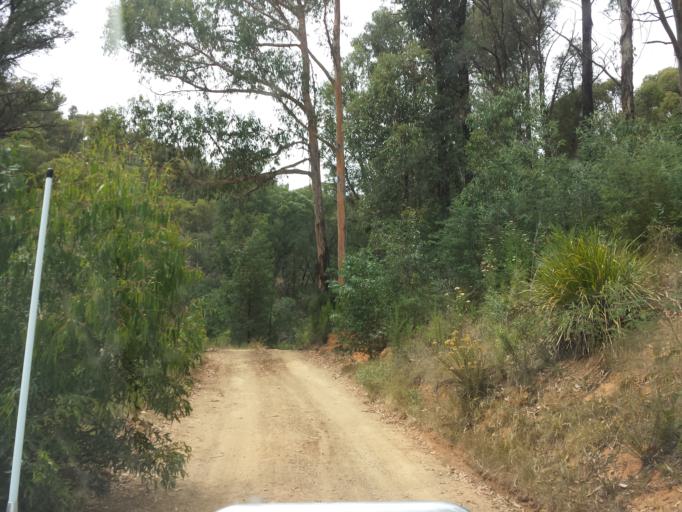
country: AU
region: Victoria
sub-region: Wellington
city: Heyfield
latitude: -37.7540
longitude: 146.5013
